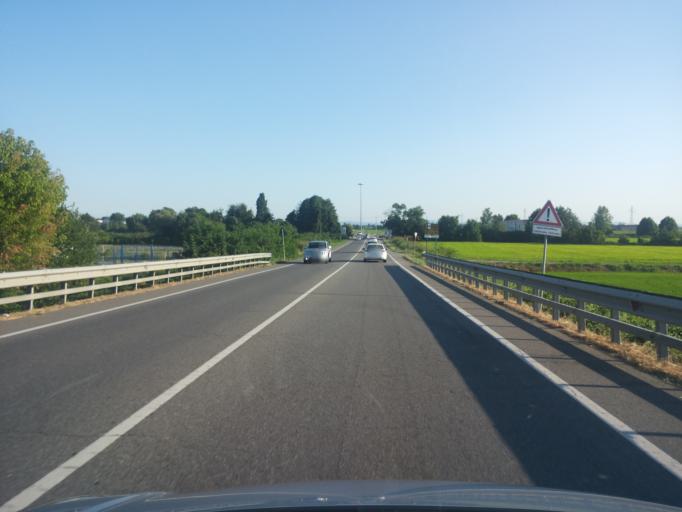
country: IT
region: Piedmont
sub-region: Provincia di Vercelli
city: Caresanablot
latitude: 45.3268
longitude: 8.3889
